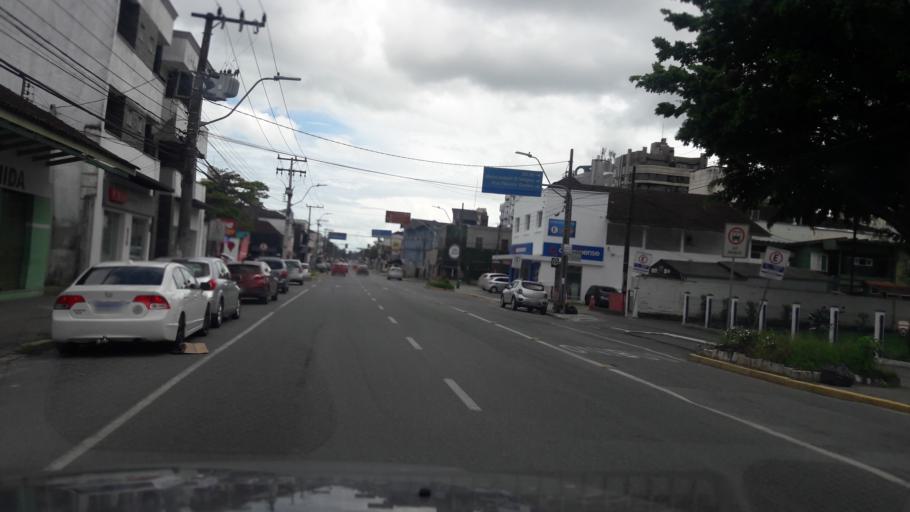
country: BR
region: Santa Catarina
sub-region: Joinville
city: Joinville
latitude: -26.3096
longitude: -48.8455
